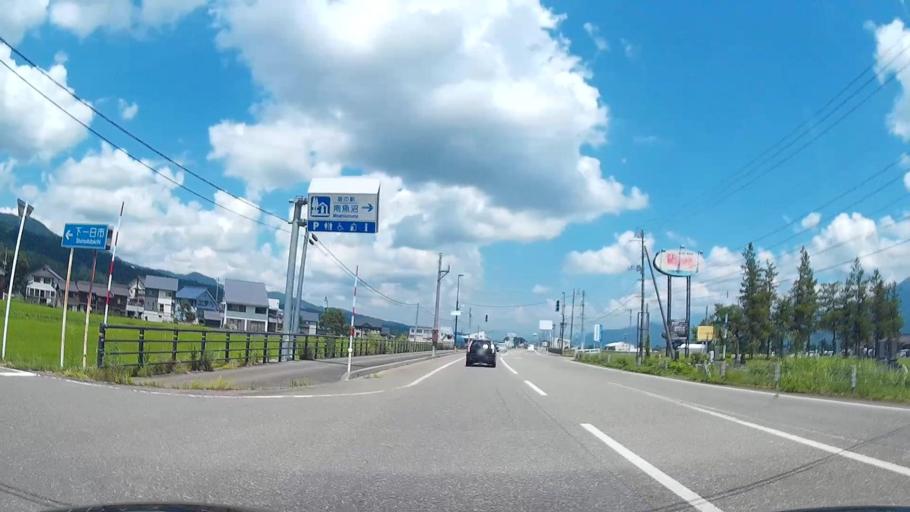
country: JP
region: Niigata
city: Shiozawa
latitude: 37.0032
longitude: 138.8168
